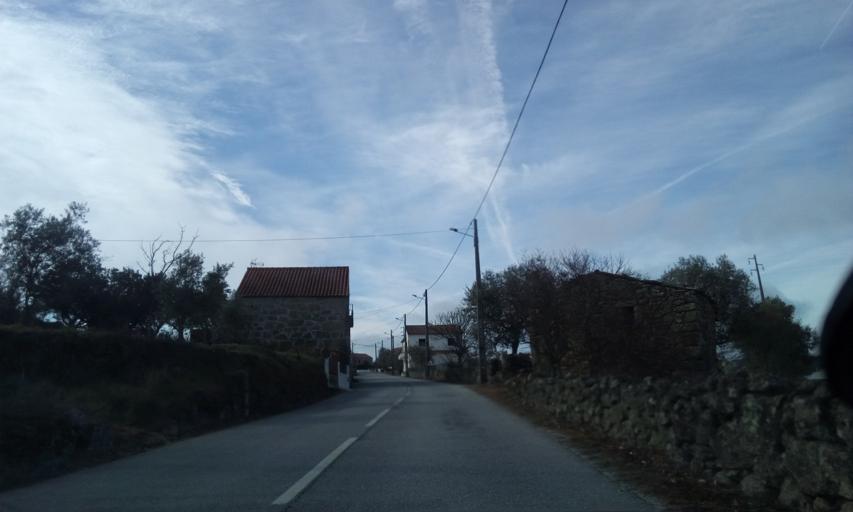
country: PT
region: Guarda
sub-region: Fornos de Algodres
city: Fornos de Algodres
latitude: 40.6582
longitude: -7.5335
